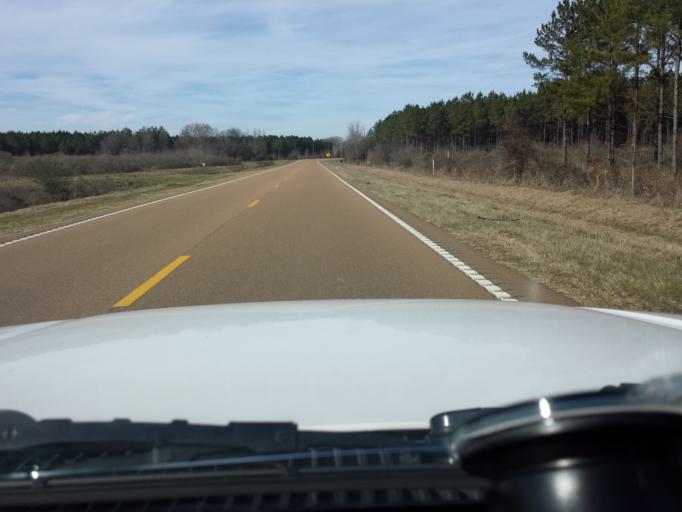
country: US
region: Mississippi
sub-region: Madison County
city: Canton
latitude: 32.7006
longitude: -90.0857
